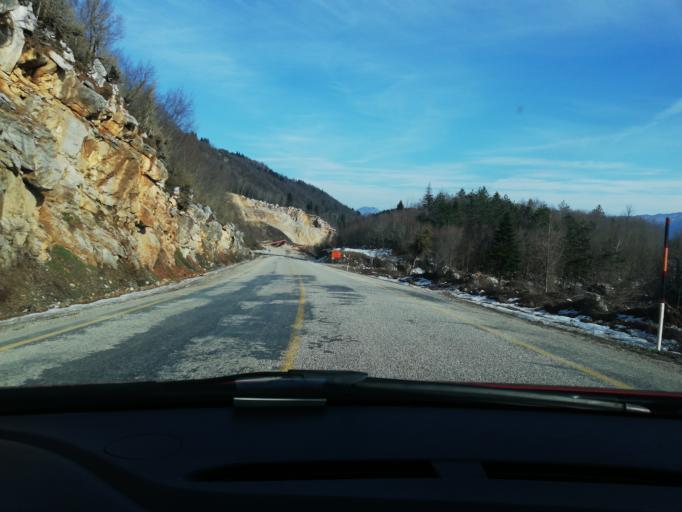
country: TR
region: Kastamonu
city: Senpazar
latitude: 41.8118
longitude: 33.1102
